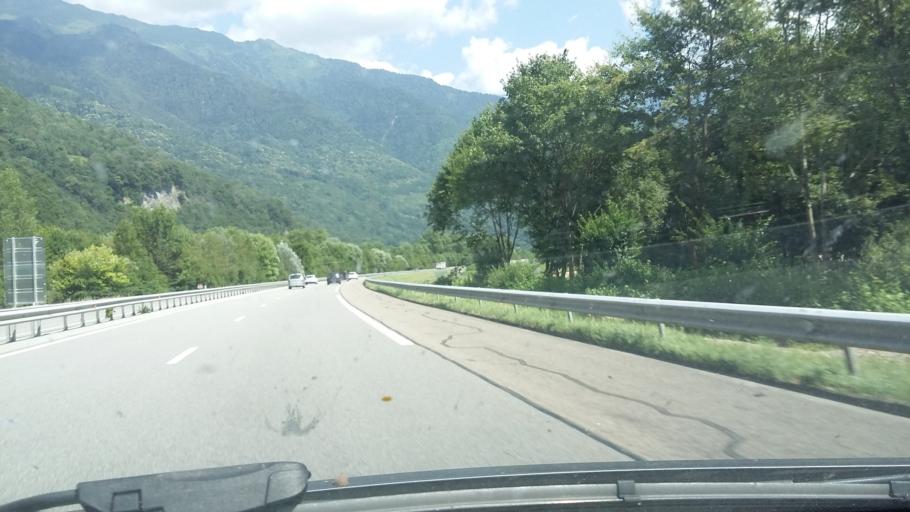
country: FR
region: Rhone-Alpes
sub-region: Departement de la Savoie
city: Aiton
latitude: 45.5592
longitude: 6.2773
